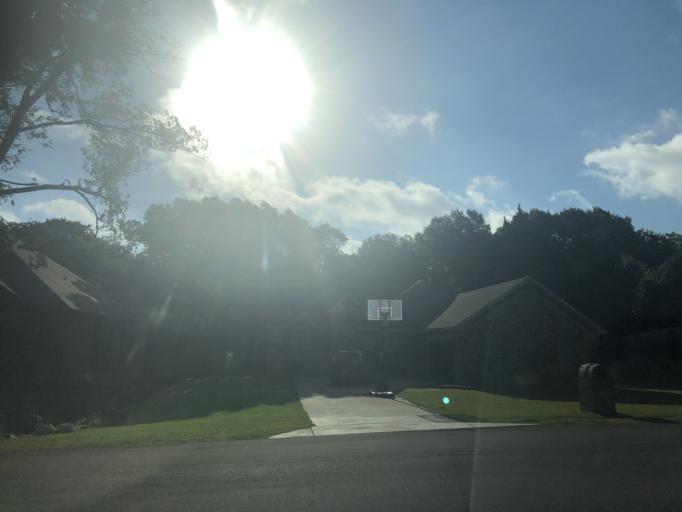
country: US
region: Texas
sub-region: Dallas County
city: Duncanville
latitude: 32.6697
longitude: -96.9170
